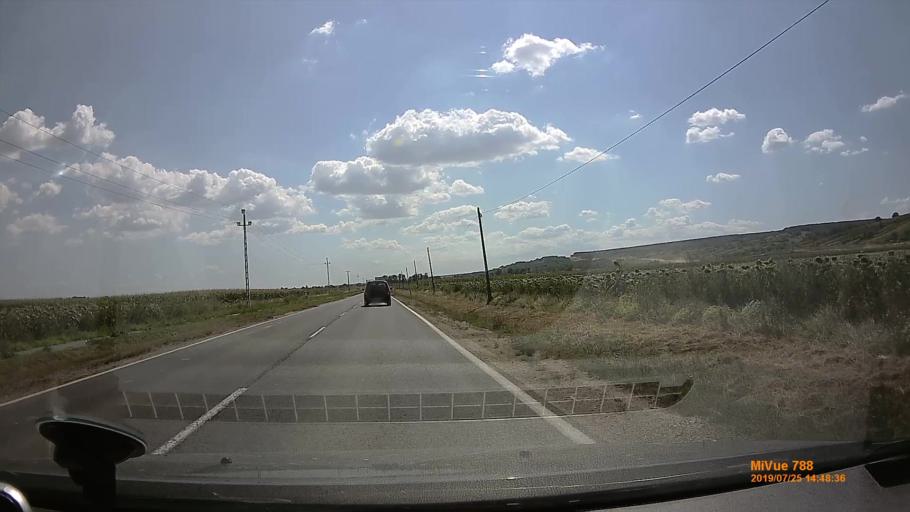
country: HU
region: Borsod-Abauj-Zemplen
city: Aszalo
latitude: 48.2359
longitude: 20.9645
